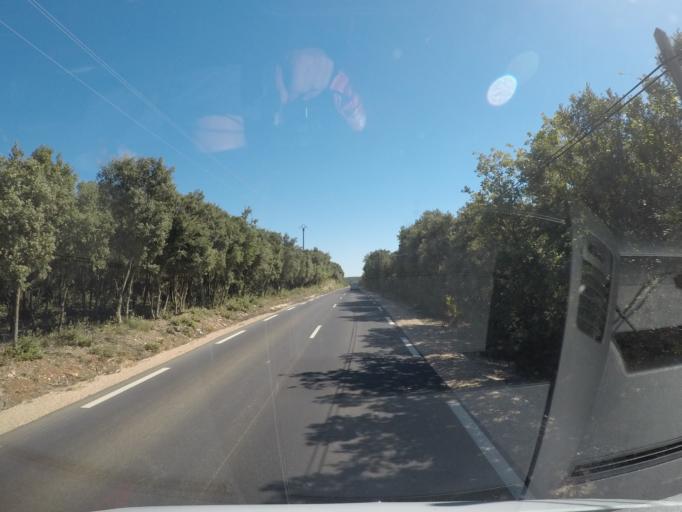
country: FR
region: Languedoc-Roussillon
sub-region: Departement de l'Herault
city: Aniane
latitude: 43.7280
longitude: 3.6425
